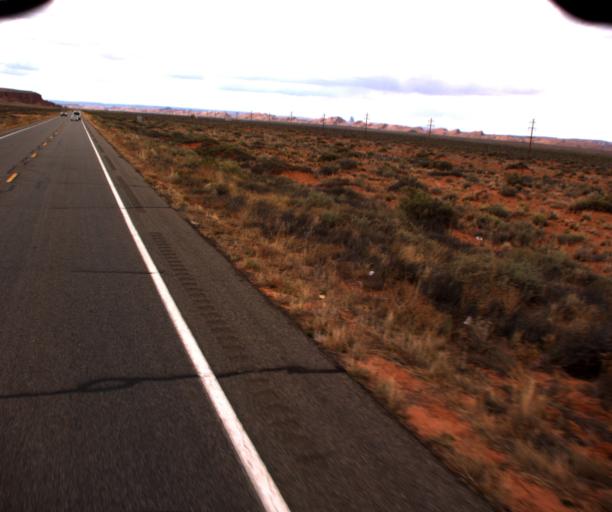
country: US
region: Arizona
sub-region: Navajo County
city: Kayenta
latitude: 36.7845
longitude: -109.9704
